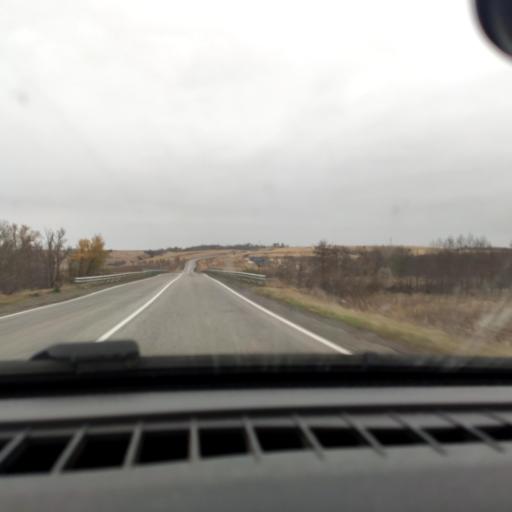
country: RU
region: Voronezj
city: Uryv-Pokrovka
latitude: 51.1296
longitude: 39.0429
